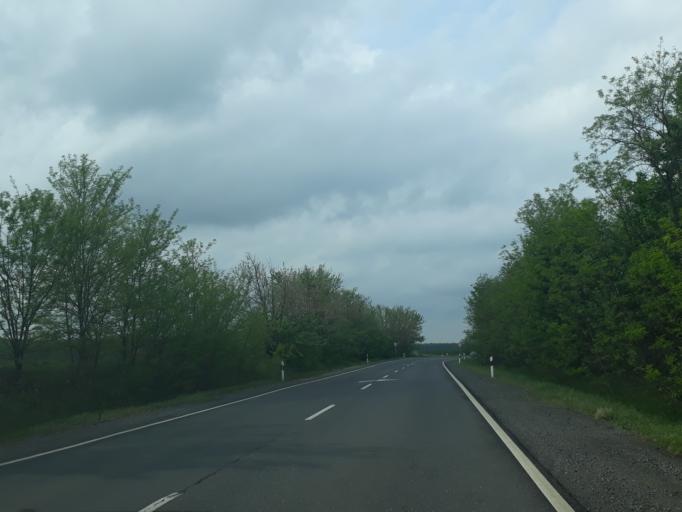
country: HU
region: Szabolcs-Szatmar-Bereg
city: Patroha
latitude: 48.1572
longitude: 22.0278
